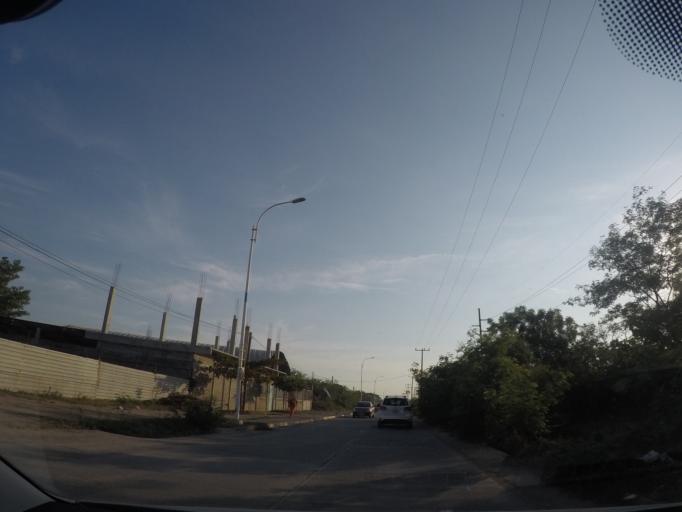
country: MX
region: Oaxaca
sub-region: Salina Cruz
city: Salina Cruz
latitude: 16.2167
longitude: -95.1911
